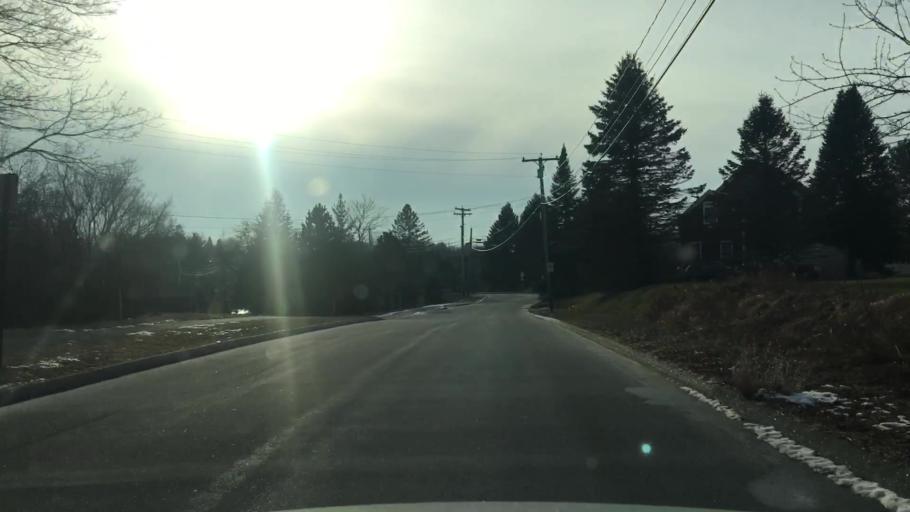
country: US
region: Maine
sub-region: Cumberland County
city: Yarmouth
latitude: 43.8089
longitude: -70.1889
